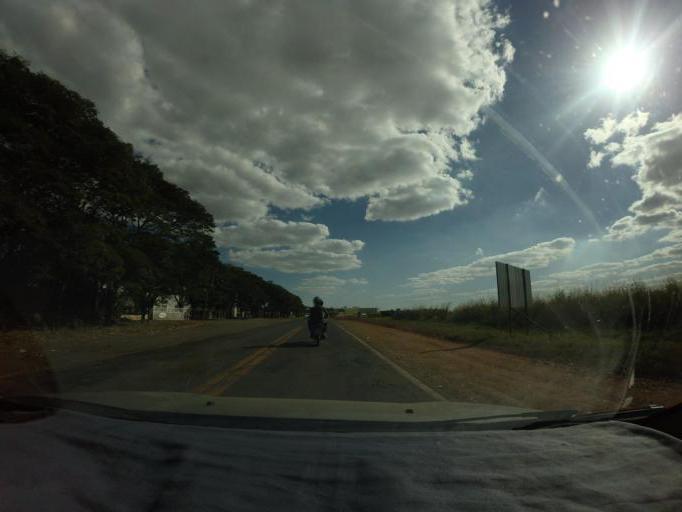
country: BR
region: Sao Paulo
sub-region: Piracicaba
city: Piracicaba
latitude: -22.7368
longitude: -47.5622
